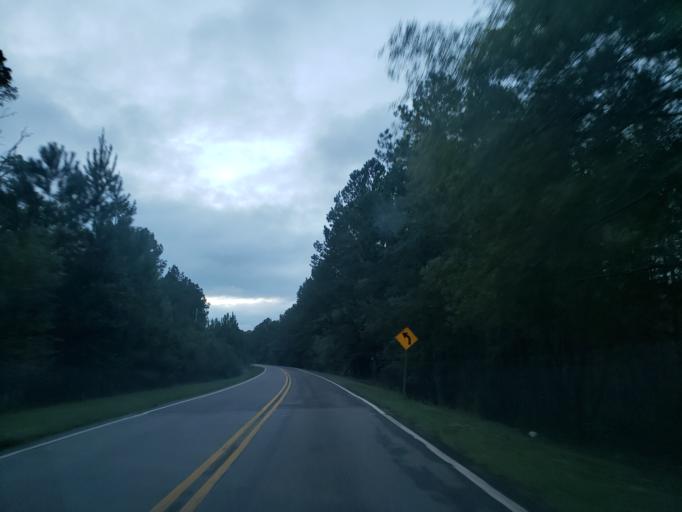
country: US
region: Georgia
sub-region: Chatham County
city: Bloomingdale
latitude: 32.0616
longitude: -81.3142
